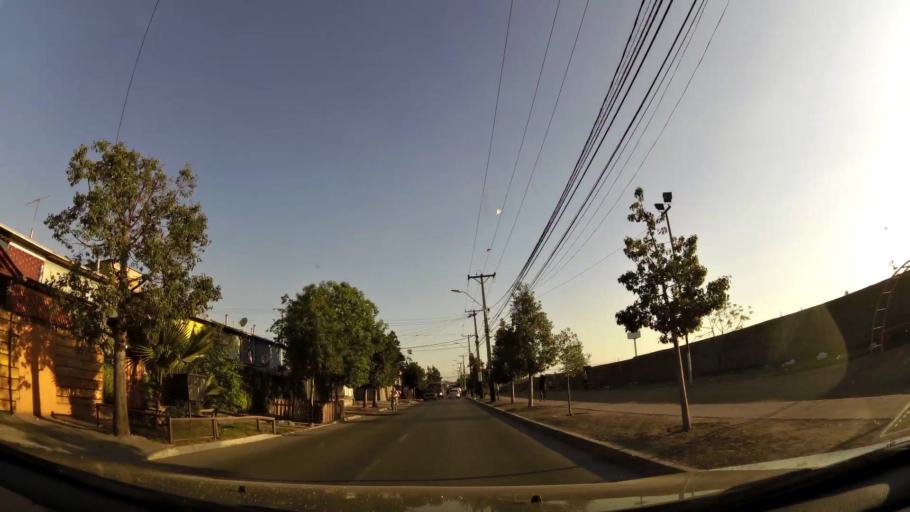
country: CL
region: Santiago Metropolitan
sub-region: Provincia de Maipo
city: San Bernardo
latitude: -33.5936
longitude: -70.6720
